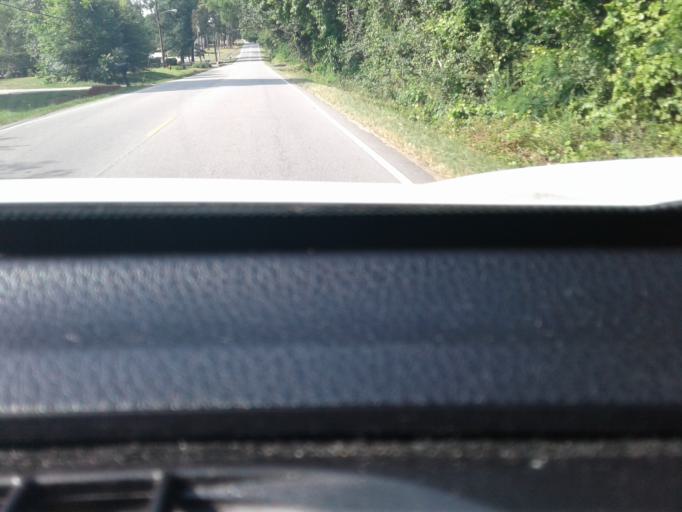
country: US
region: North Carolina
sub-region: Johnston County
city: Benson
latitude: 35.3945
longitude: -78.5432
